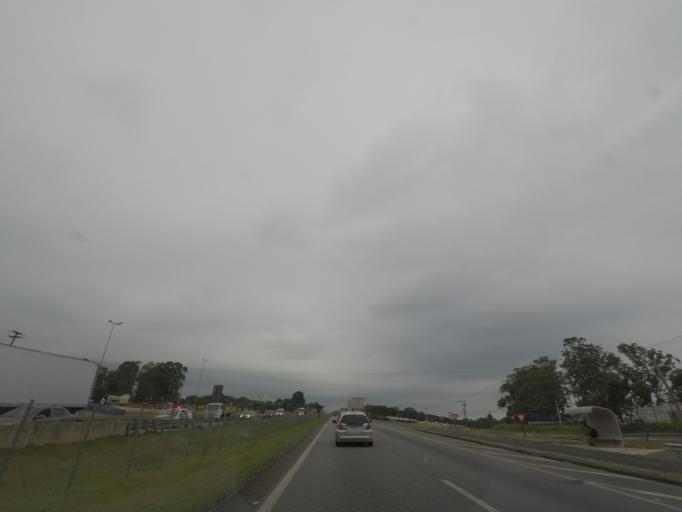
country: BR
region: Sao Paulo
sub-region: Jarinu
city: Jarinu
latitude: -23.0556
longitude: -46.6599
